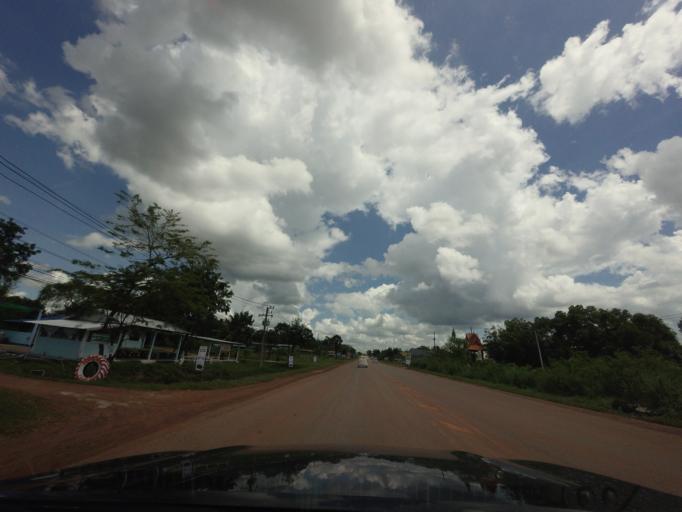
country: TH
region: Changwat Udon Thani
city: Ban Dung
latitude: 17.6780
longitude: 103.2439
